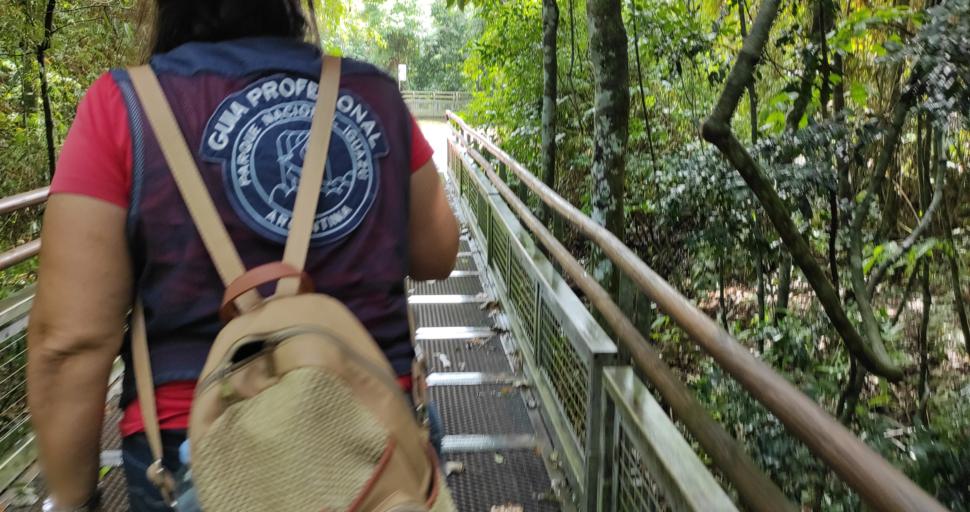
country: AR
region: Misiones
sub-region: Departamento de Iguazu
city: Puerto Iguazu
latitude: -25.7016
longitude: -54.4447
